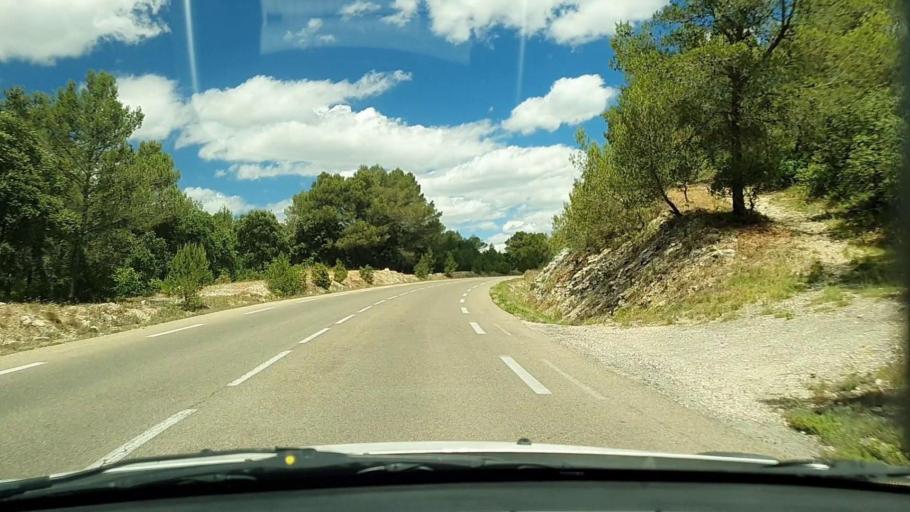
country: FR
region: Languedoc-Roussillon
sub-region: Departement du Gard
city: Poulx
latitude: 43.8838
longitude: 4.4166
